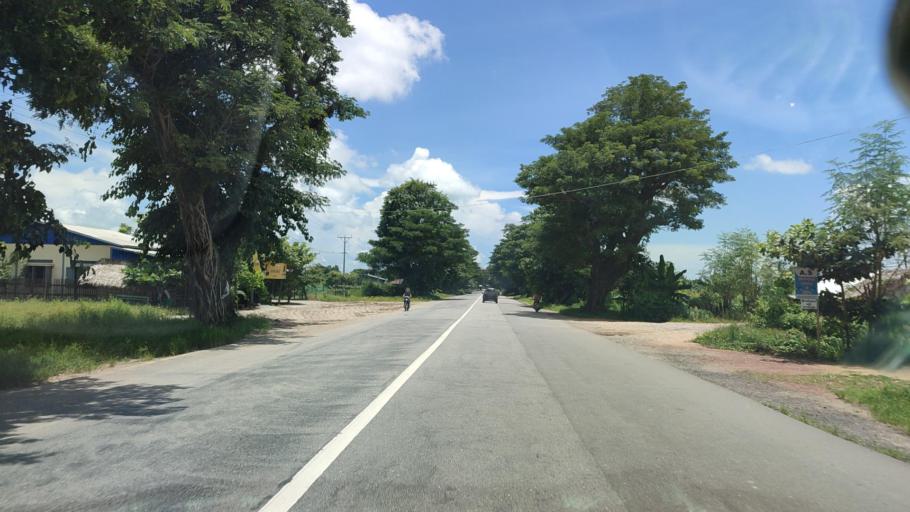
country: MM
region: Bago
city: Pyu
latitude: 18.3681
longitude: 96.4782
